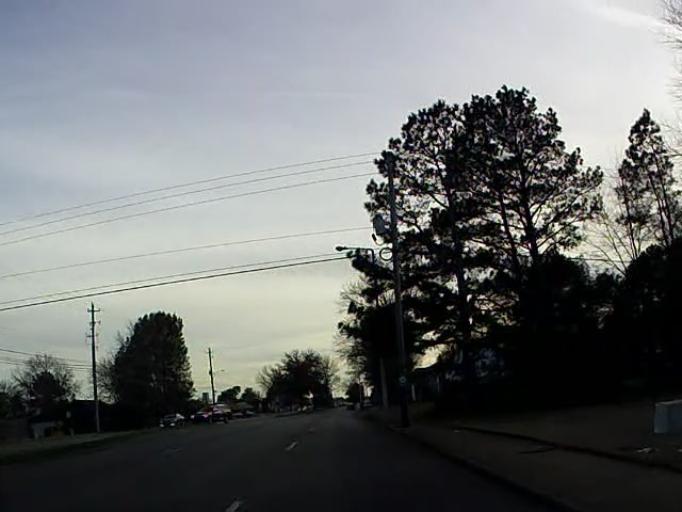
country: US
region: Tennessee
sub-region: Shelby County
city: Germantown
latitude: 35.0573
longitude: -89.8439
